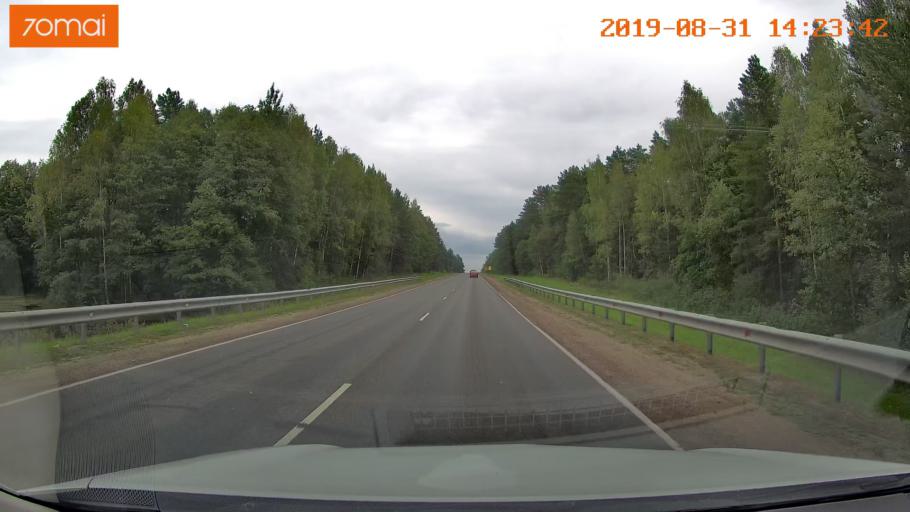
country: RU
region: Smolensk
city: Yekimovichi
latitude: 54.0981
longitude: 33.2394
